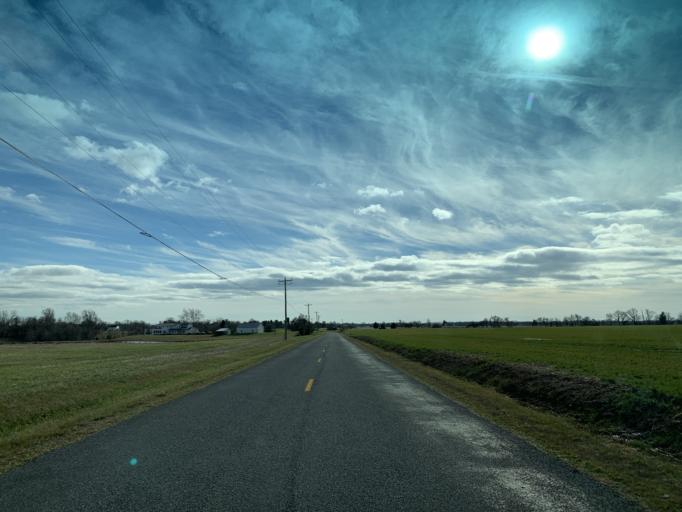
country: US
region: Maryland
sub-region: Kent County
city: Chestertown
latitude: 39.3471
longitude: -76.0539
